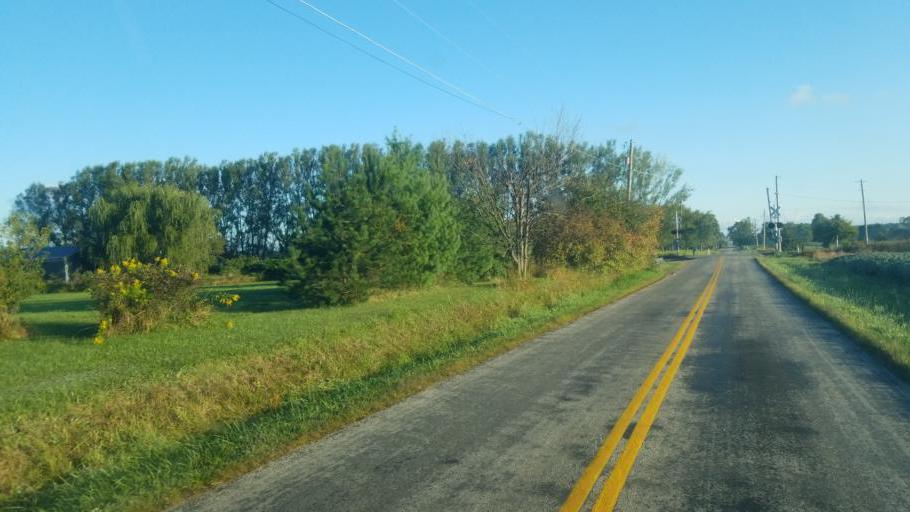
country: US
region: Ohio
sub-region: Lorain County
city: Wellington
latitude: 41.0317
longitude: -82.2599
